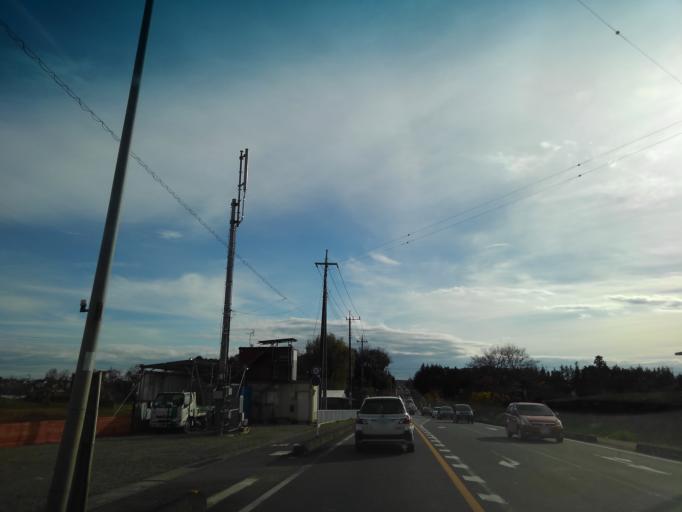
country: JP
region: Saitama
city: Hanno
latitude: 35.8649
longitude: 139.3360
